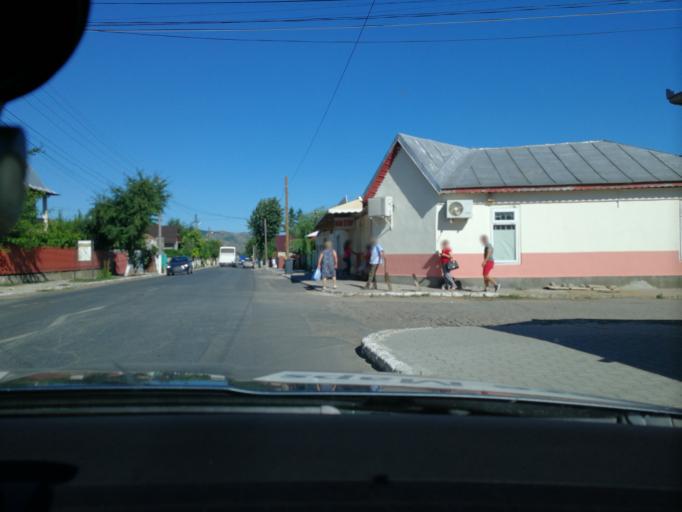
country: RO
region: Tulcea
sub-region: Oras Macin
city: Macin
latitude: 45.2433
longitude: 28.1365
